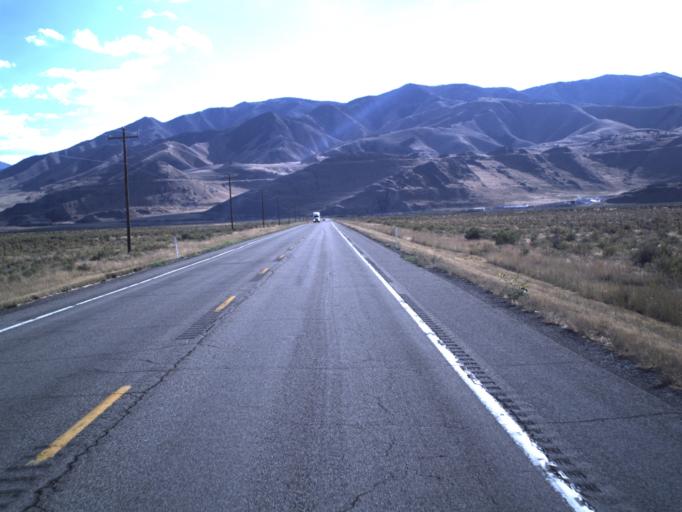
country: US
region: Utah
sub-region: Tooele County
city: Grantsville
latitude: 40.6924
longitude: -112.5351
